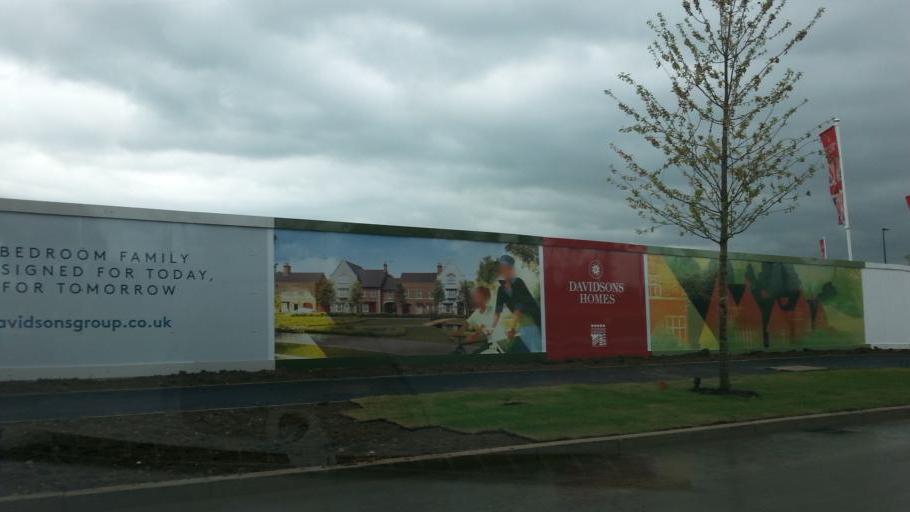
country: GB
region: England
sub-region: Warwickshire
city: Rugby
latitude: 52.3578
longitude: -1.1889
